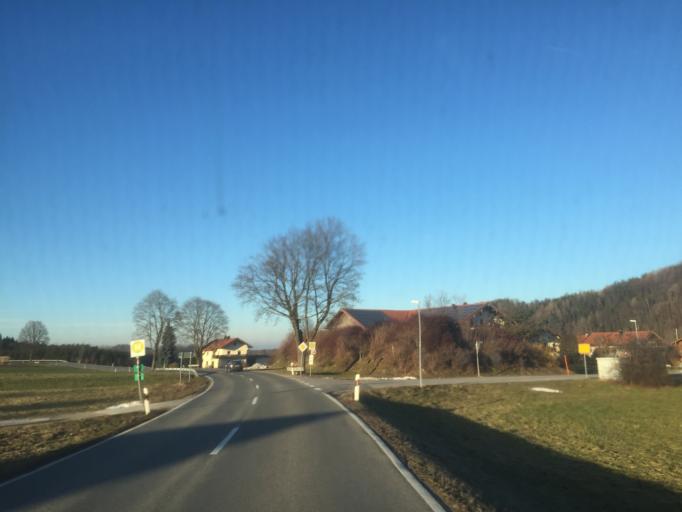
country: DE
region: Bavaria
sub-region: Upper Bavaria
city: Siegsdorf
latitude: 47.8373
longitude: 12.6355
